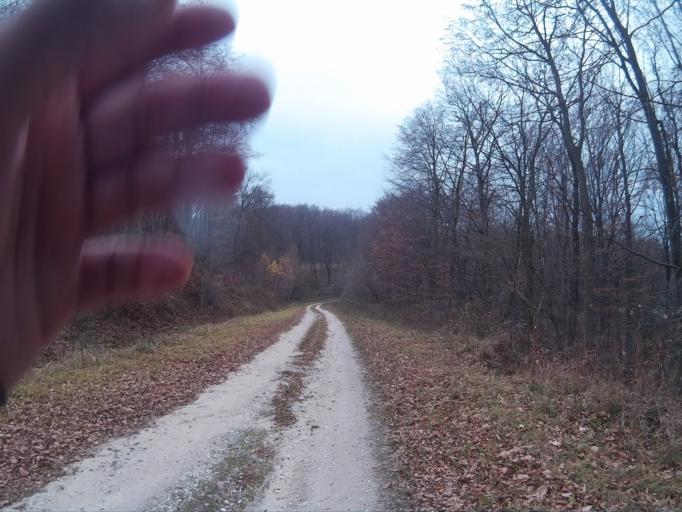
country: HU
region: Veszprem
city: Tapolca
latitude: 46.9744
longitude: 17.5063
